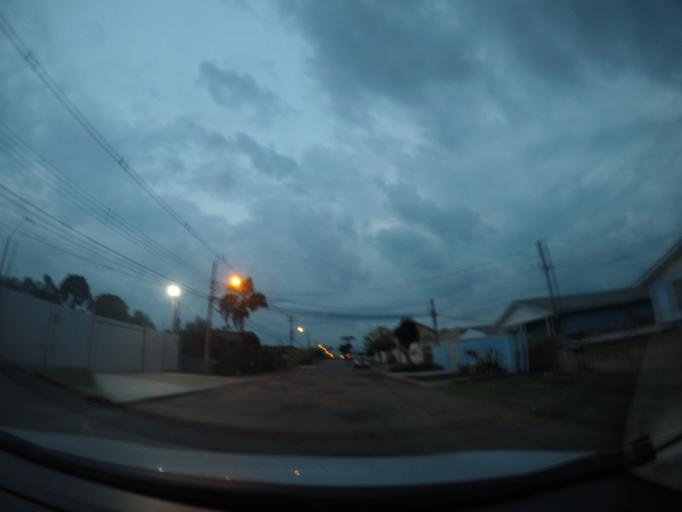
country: BR
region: Parana
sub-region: Sao Jose Dos Pinhais
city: Sao Jose dos Pinhais
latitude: -25.5040
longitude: -49.2309
